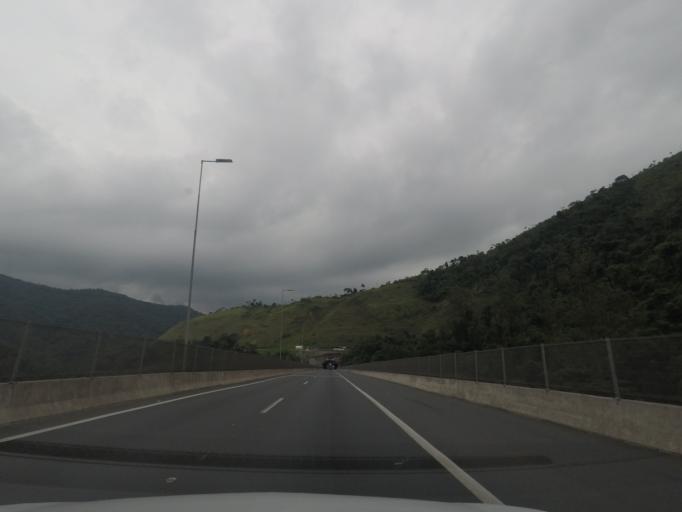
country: BR
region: Sao Paulo
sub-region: Miracatu
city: Miracatu
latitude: -24.1138
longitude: -47.2688
